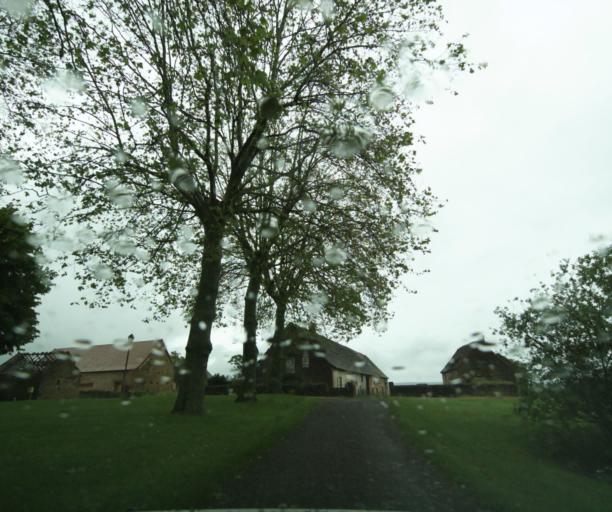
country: FR
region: Bourgogne
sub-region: Departement de Saone-et-Loire
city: Charolles
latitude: 46.4752
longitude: 4.2964
